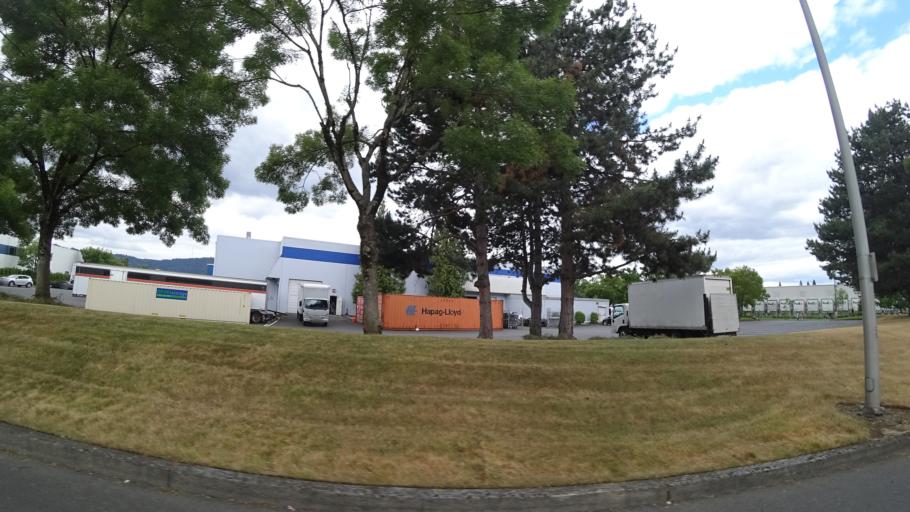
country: US
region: Oregon
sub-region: Multnomah County
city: Portland
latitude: 45.5704
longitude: -122.7027
